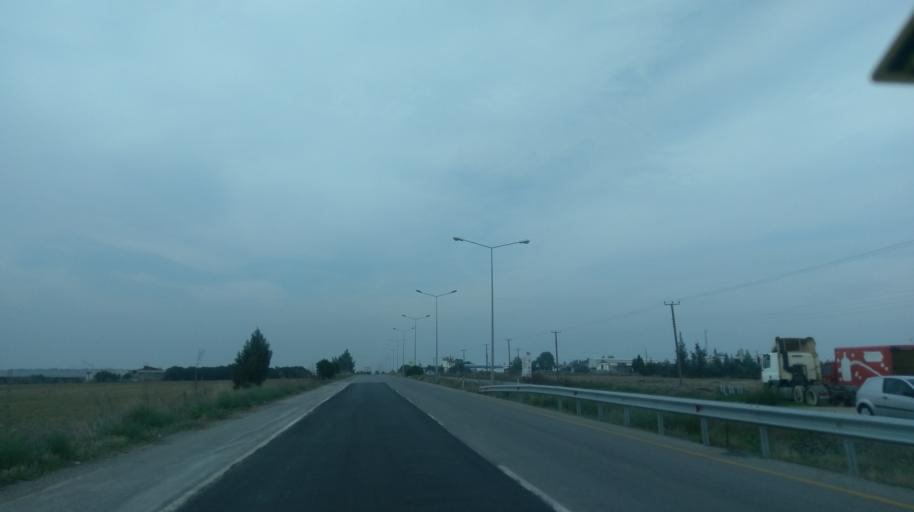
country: CY
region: Lefkosia
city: Mammari
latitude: 35.2125
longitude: 33.2620
